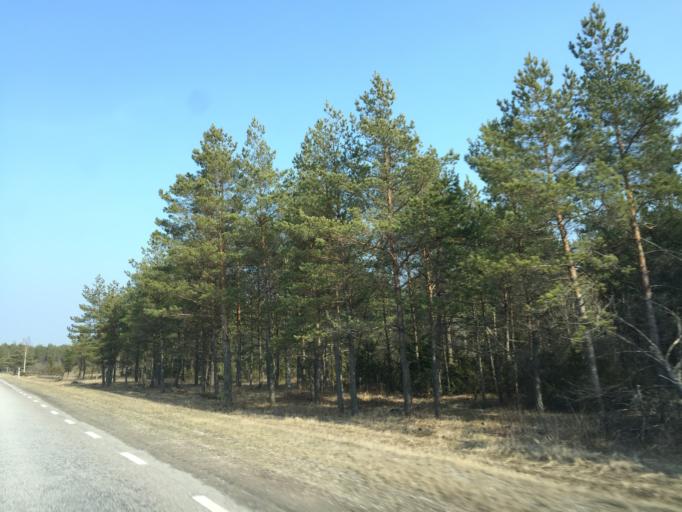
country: EE
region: Saare
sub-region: Kuressaare linn
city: Kuressaare
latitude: 58.3793
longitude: 22.7351
